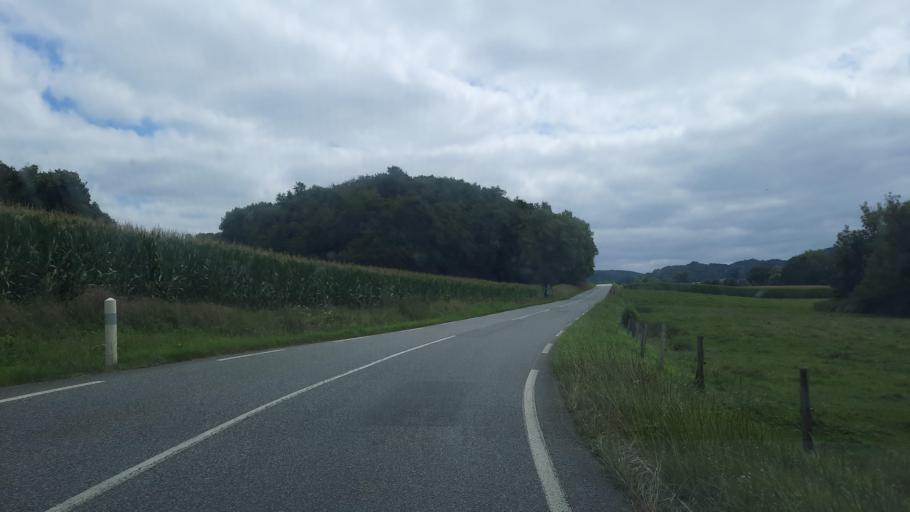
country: FR
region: Midi-Pyrenees
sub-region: Departement des Hautes-Pyrenees
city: Trie-sur-Baise
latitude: 43.3046
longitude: 0.2696
